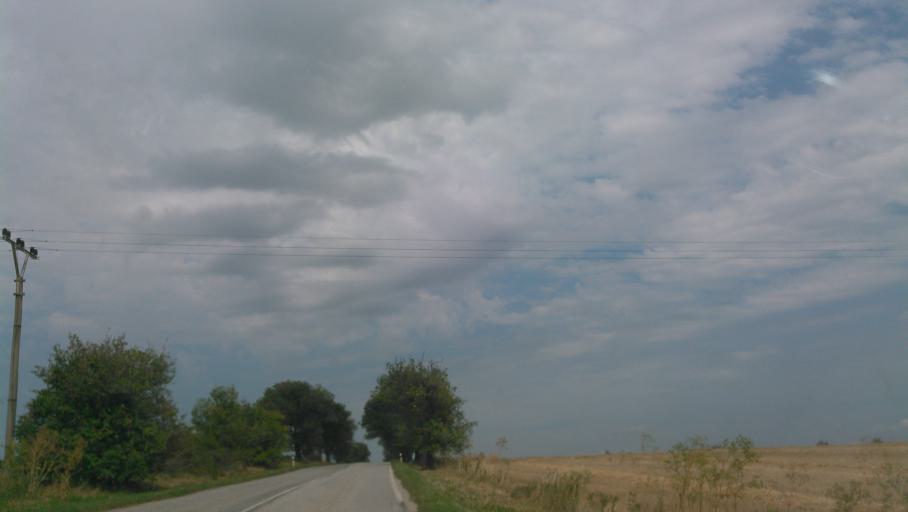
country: SK
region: Trnavsky
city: Hlohovec
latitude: 48.4496
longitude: 17.9135
